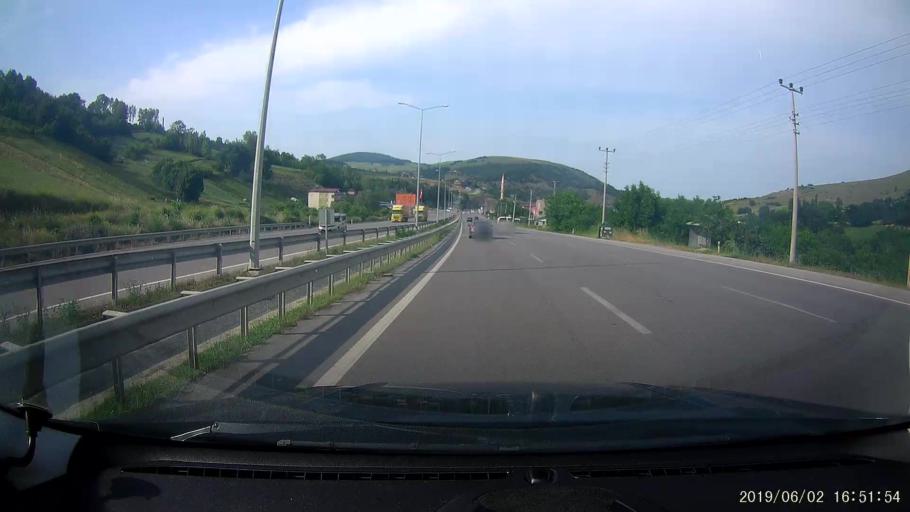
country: TR
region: Samsun
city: Samsun
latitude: 41.2797
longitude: 36.1900
